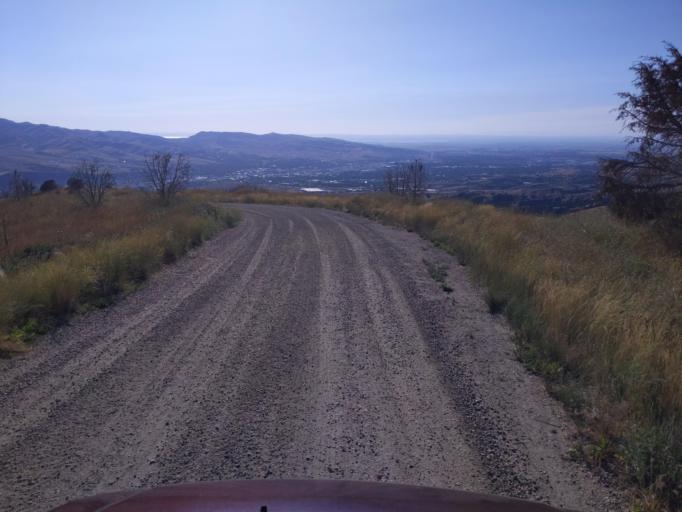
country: US
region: Idaho
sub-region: Bannock County
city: Pocatello
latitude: 42.8504
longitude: -112.3726
